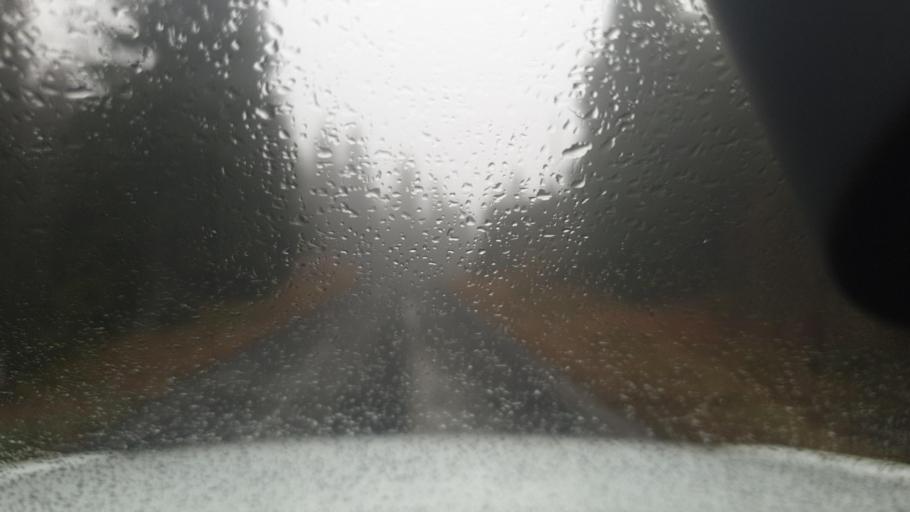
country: SE
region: Vaermland
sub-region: Torsby Kommun
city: Torsby
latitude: 60.1702
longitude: 12.6249
